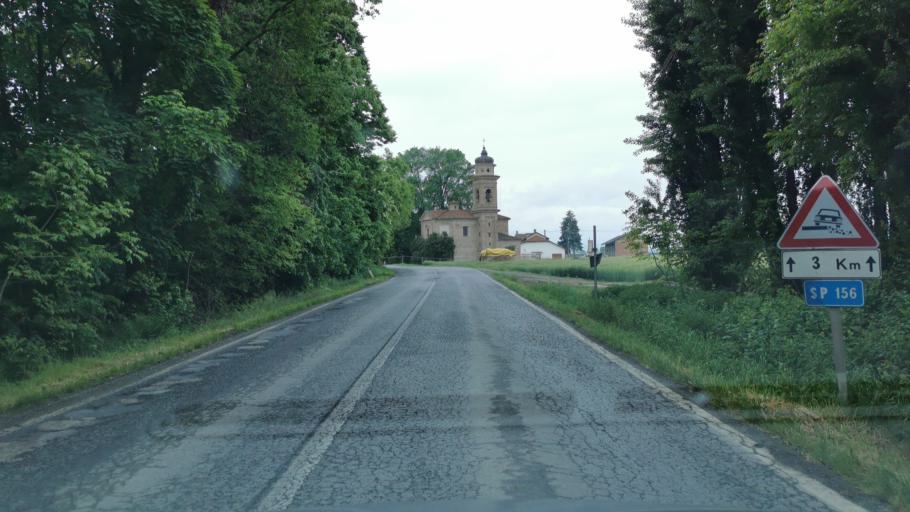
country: IT
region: Piedmont
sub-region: Provincia di Cuneo
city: Genola
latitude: 44.6105
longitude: 7.6196
